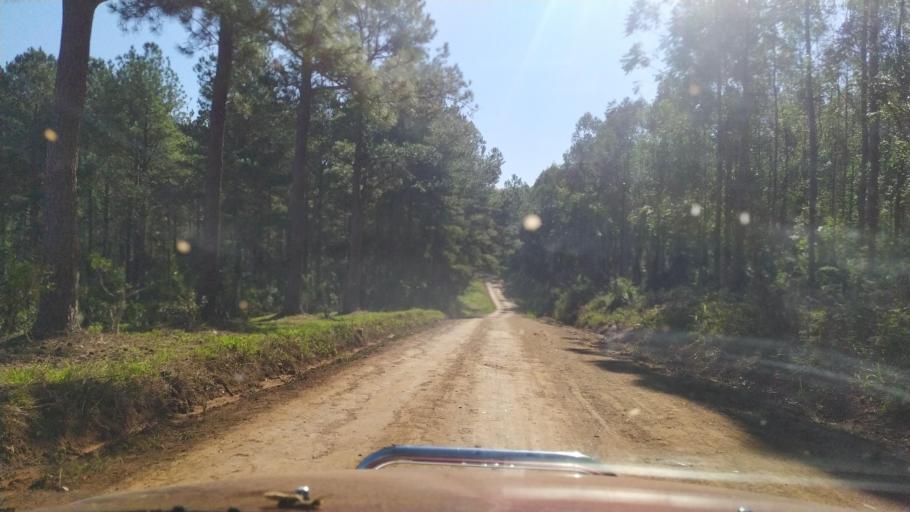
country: AR
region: Misiones
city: El Alcazar
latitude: -26.7222
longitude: -54.6864
